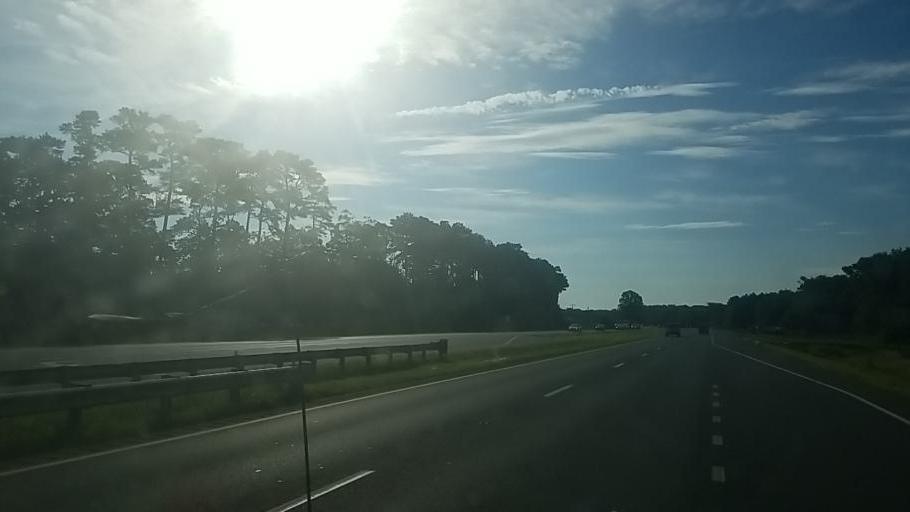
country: US
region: Maryland
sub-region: Worcester County
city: West Ocean City
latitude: 38.3400
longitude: -75.1541
